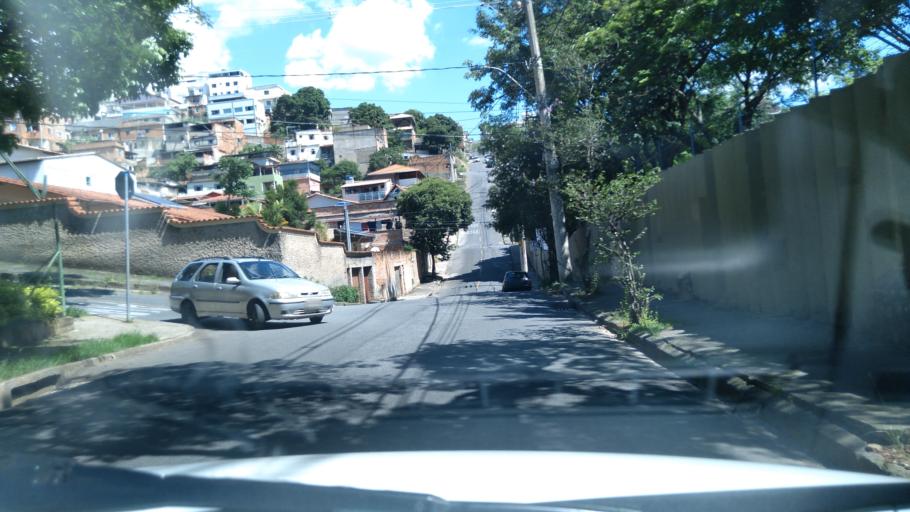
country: BR
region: Minas Gerais
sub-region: Belo Horizonte
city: Belo Horizonte
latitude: -19.8739
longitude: -43.9142
